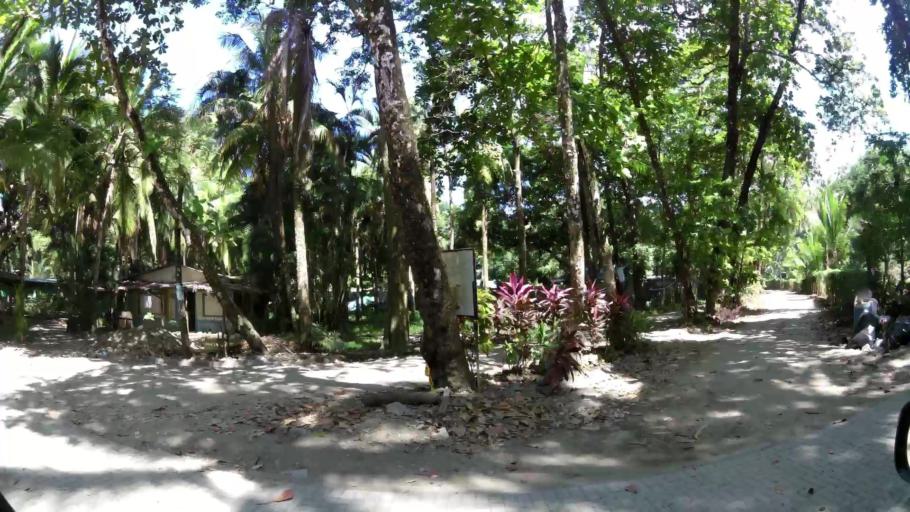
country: CR
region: San Jose
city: San Isidro
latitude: 9.2525
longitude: -83.8655
